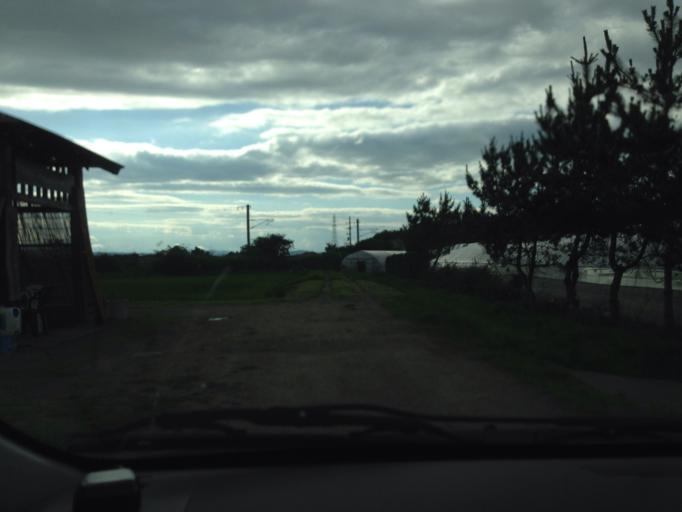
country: JP
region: Fukushima
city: Kitakata
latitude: 37.5299
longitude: 139.9251
